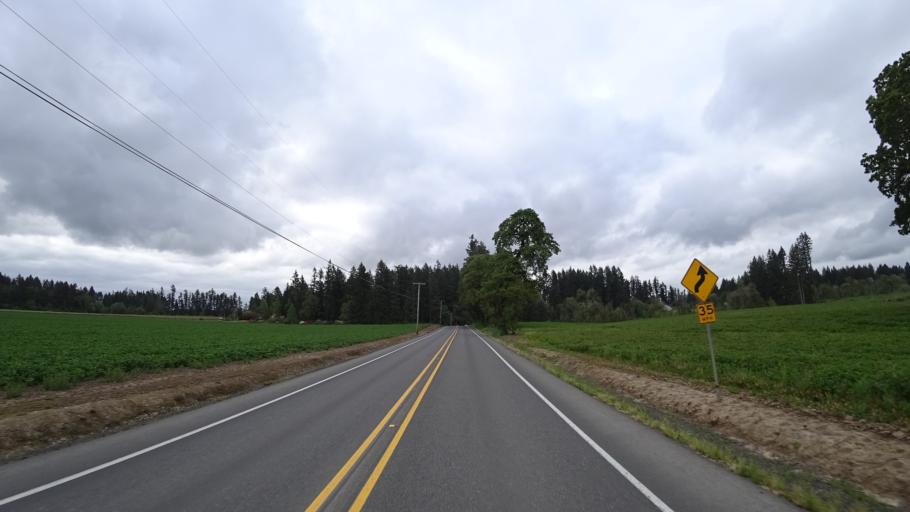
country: US
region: Oregon
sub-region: Washington County
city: North Plains
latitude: 45.5680
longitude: -122.9704
